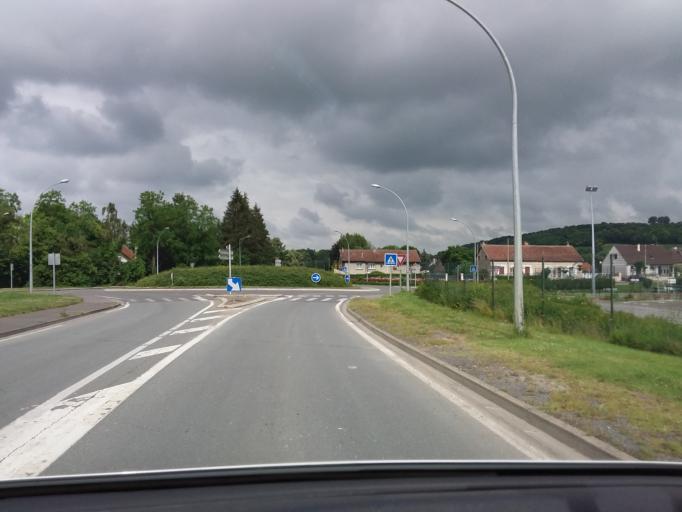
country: FR
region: Picardie
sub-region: Departement de l'Aisne
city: Bucy-le-Long
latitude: 49.3875
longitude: 3.3937
